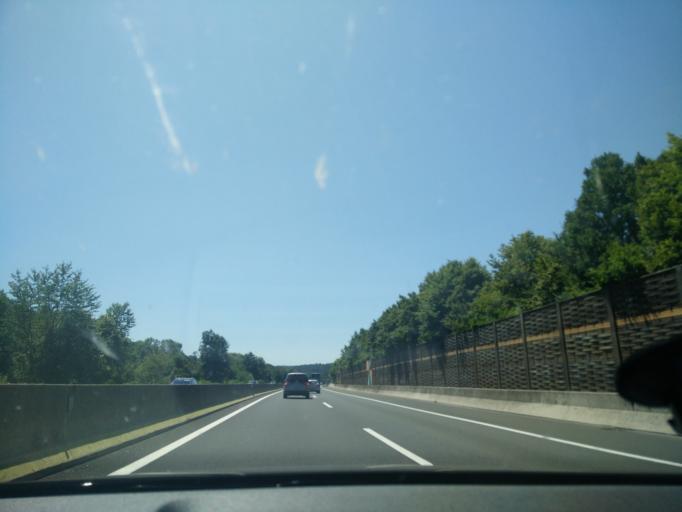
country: AT
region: Styria
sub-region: Politischer Bezirk Hartberg-Fuerstenfeld
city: Sebersdorf
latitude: 47.2172
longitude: 15.9945
